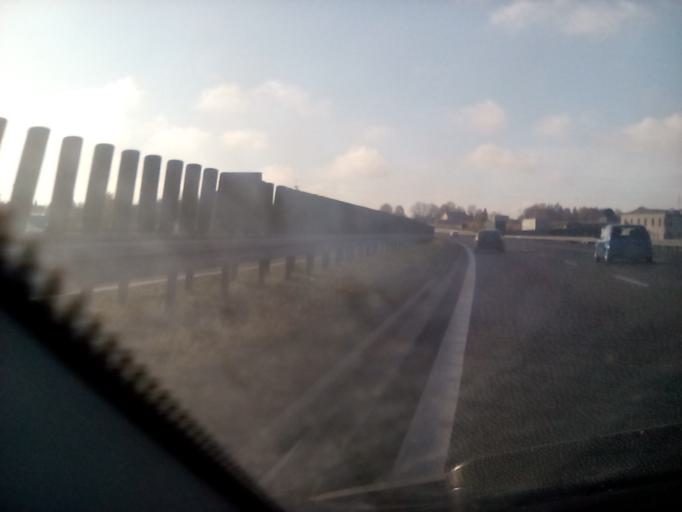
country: PL
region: Masovian Voivodeship
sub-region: Powiat grojecki
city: Grojec
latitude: 51.8693
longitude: 20.8514
